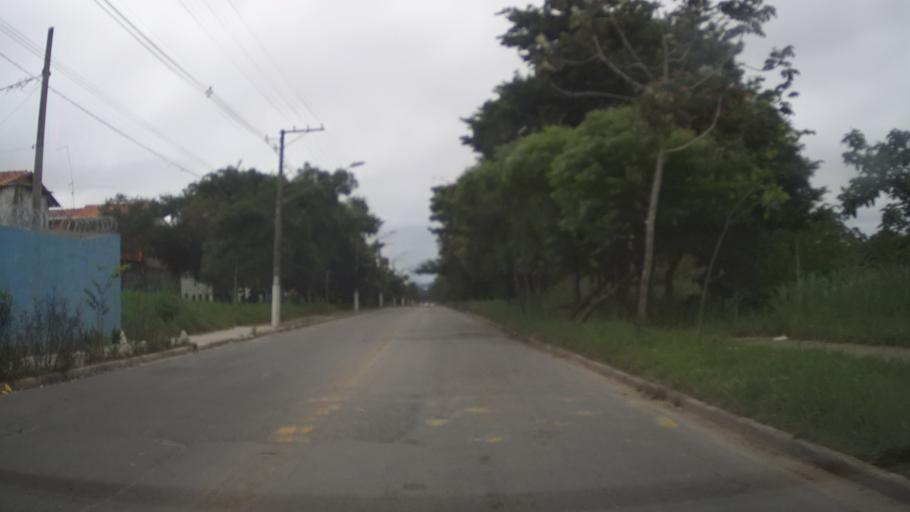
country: BR
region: Sao Paulo
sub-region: Itaquaquecetuba
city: Itaquaquecetuba
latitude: -23.4207
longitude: -46.4194
